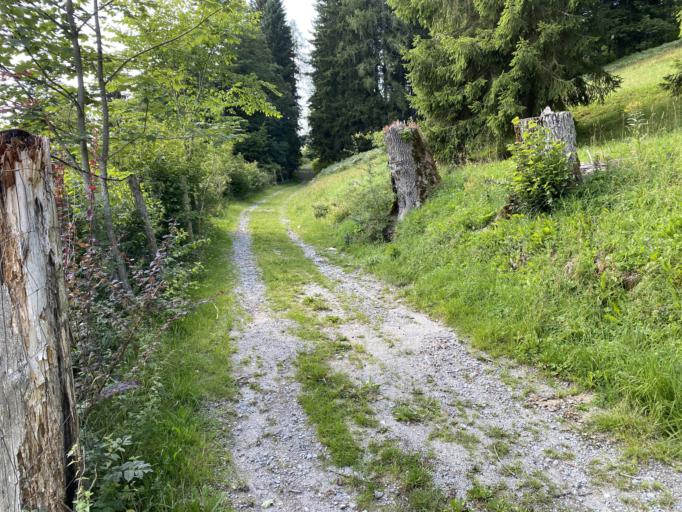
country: AT
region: Lower Austria
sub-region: Politischer Bezirk Lilienfeld
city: Annaberg
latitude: 47.8788
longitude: 15.3516
